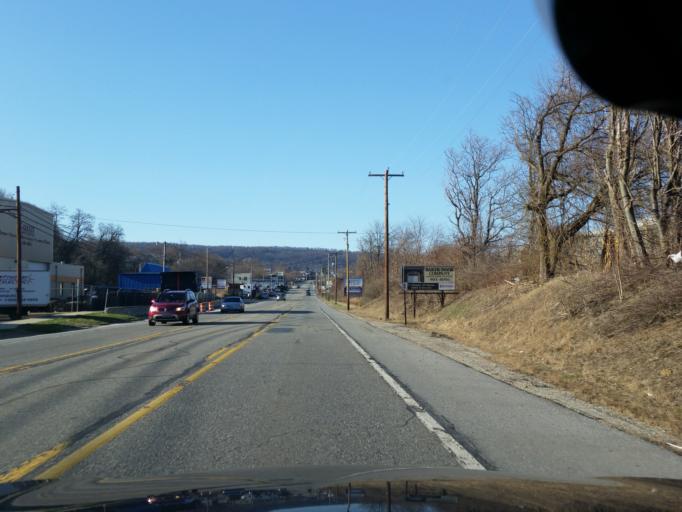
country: US
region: Pennsylvania
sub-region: Cumberland County
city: Enola
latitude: 40.2882
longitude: -76.9296
